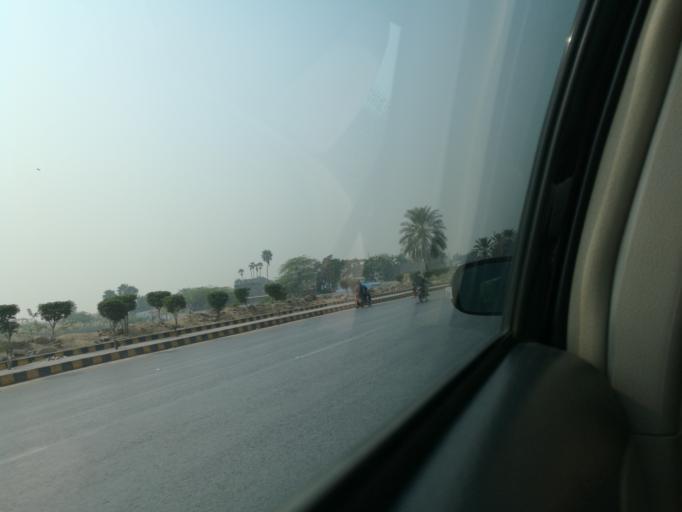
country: PK
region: Sindh
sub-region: Karachi District
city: Karachi
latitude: 24.8761
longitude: 67.1005
